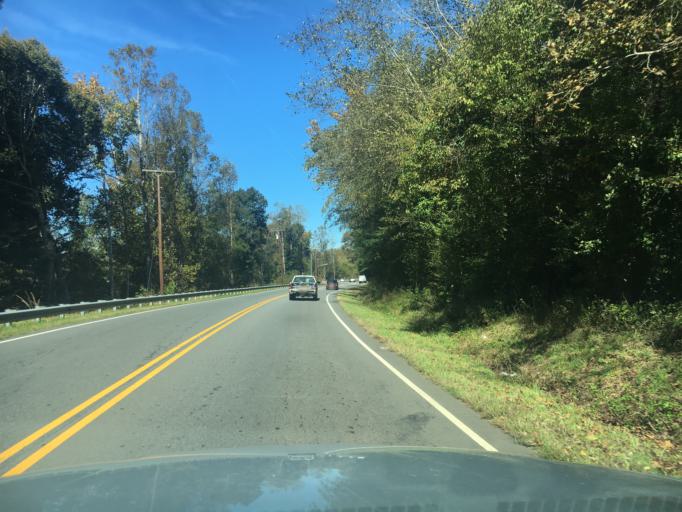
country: US
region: North Carolina
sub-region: Burke County
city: Morganton
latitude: 35.7372
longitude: -81.7099
